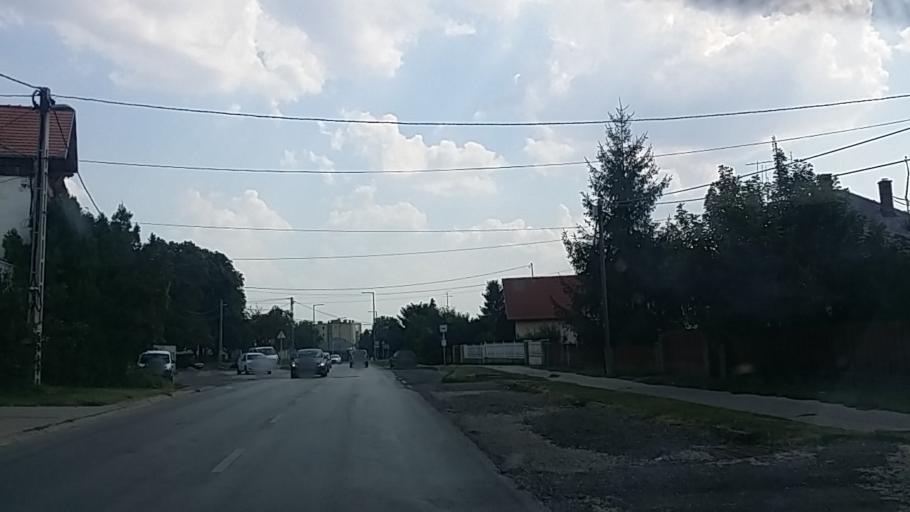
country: HU
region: Baranya
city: Pecs
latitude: 46.0700
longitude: 18.1874
